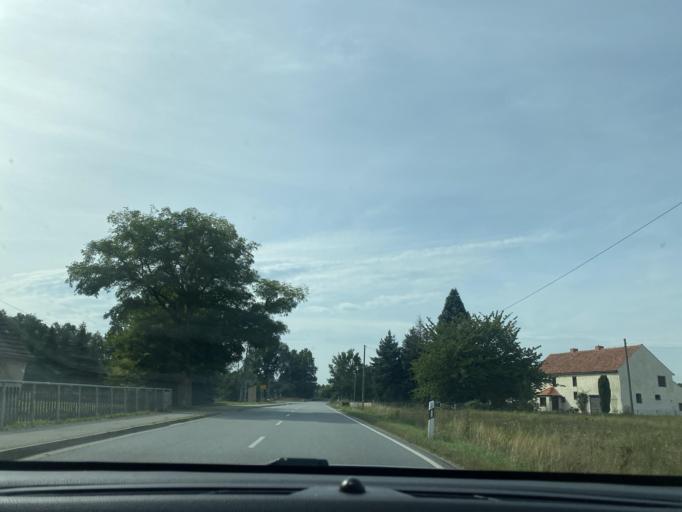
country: DE
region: Saxony
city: Quitzdorf
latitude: 51.2074
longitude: 14.7634
